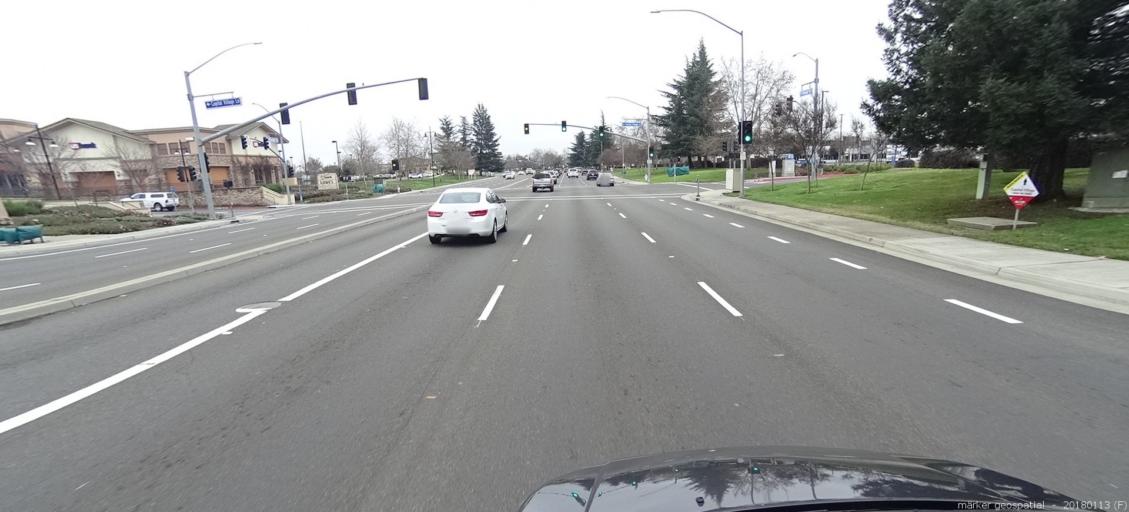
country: US
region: California
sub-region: Sacramento County
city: Rancho Cordova
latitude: 38.5844
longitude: -121.2858
